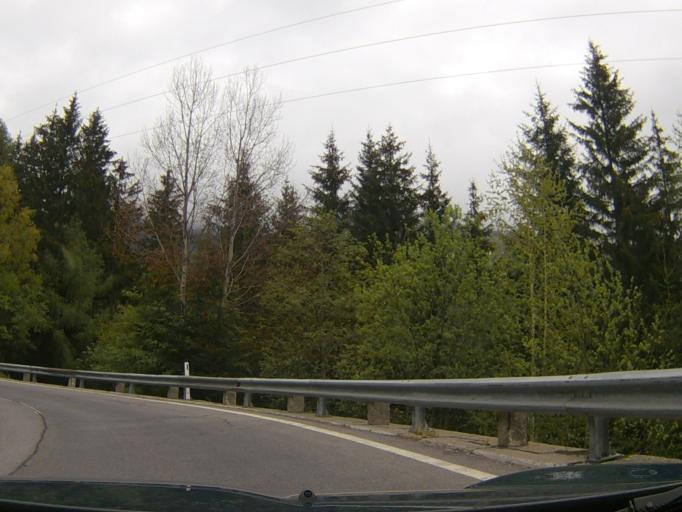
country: AT
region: Carinthia
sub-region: Politischer Bezirk Spittal an der Drau
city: Obervellach
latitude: 46.9683
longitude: 13.1853
